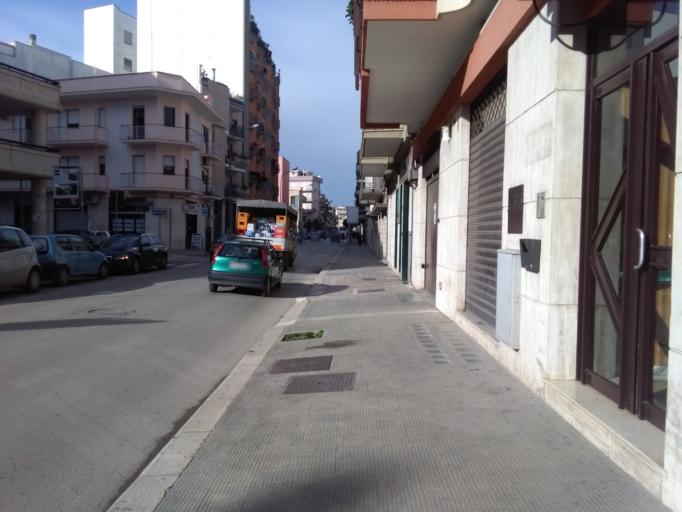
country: IT
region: Apulia
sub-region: Provincia di Barletta - Andria - Trani
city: Andria
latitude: 41.2322
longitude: 16.2997
